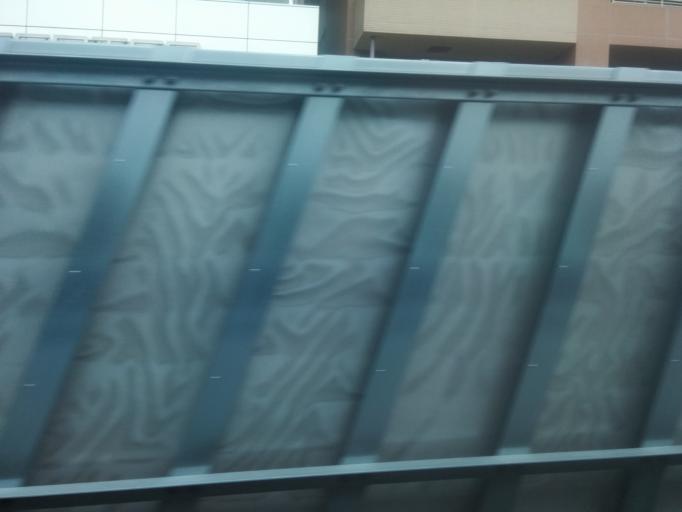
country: JP
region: Kanagawa
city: Yokohama
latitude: 35.5032
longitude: 139.6123
